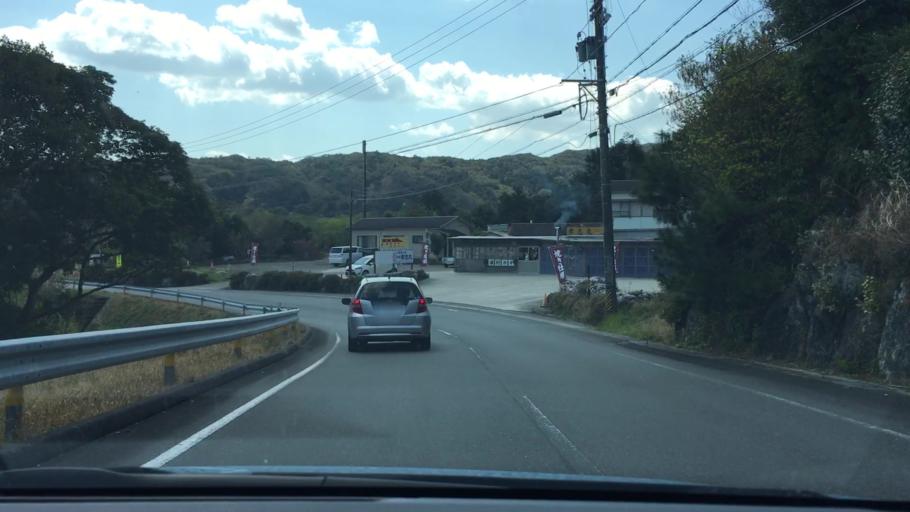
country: JP
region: Mie
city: Toba
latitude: 34.4527
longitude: 136.8745
